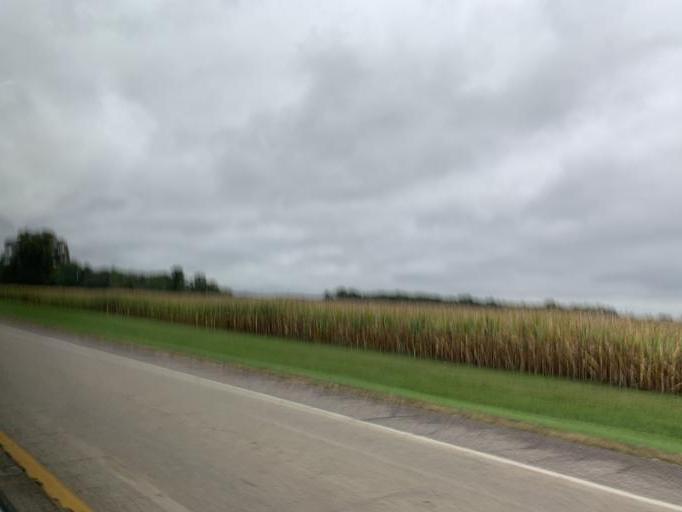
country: US
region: Wisconsin
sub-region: Sauk County
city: Sauk City
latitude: 43.2710
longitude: -89.7884
